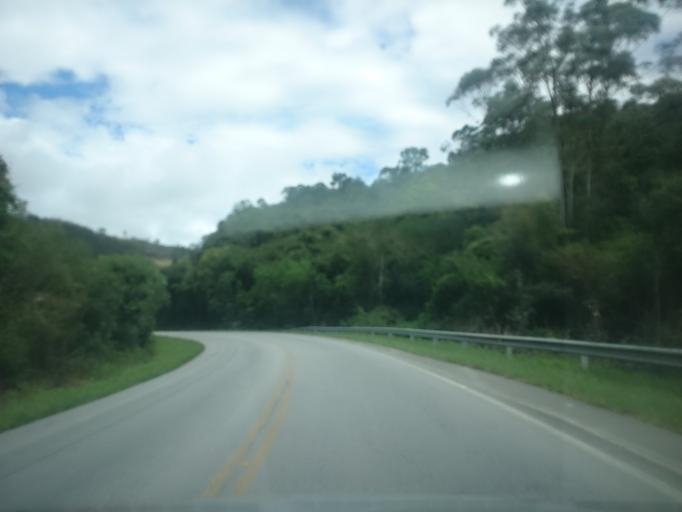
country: BR
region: Santa Catarina
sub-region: Anitapolis
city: Anitapolis
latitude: -27.6994
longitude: -49.2368
